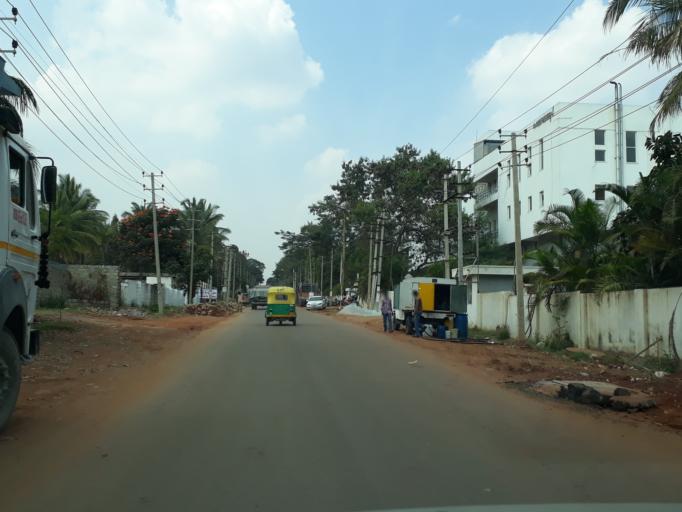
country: IN
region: Karnataka
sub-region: Bangalore Urban
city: Anekal
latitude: 12.8122
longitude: 77.6808
